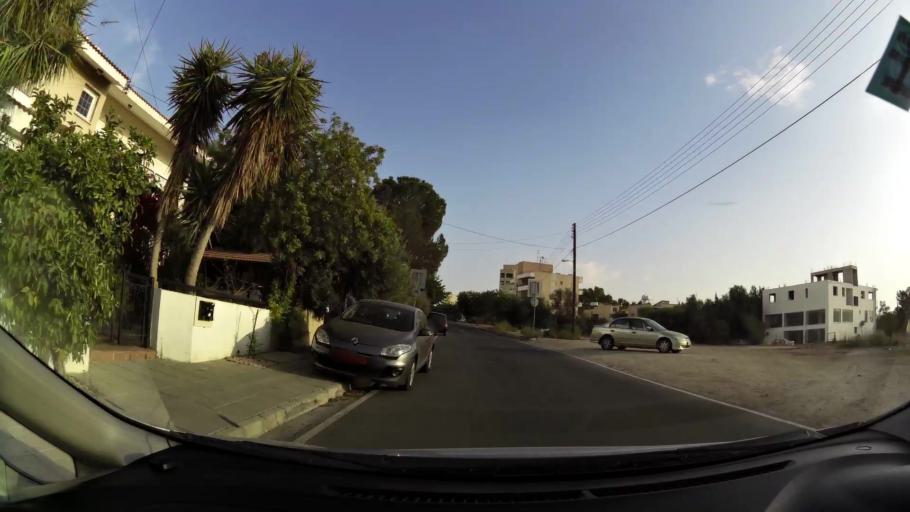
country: CY
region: Lefkosia
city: Nicosia
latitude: 35.1638
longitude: 33.3852
